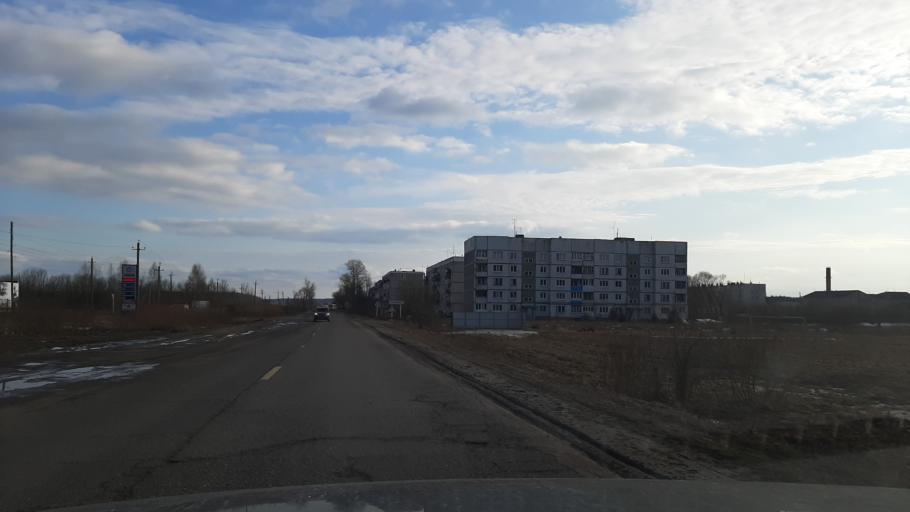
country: RU
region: Ivanovo
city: Novo-Talitsy
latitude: 56.9265
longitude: 40.7367
